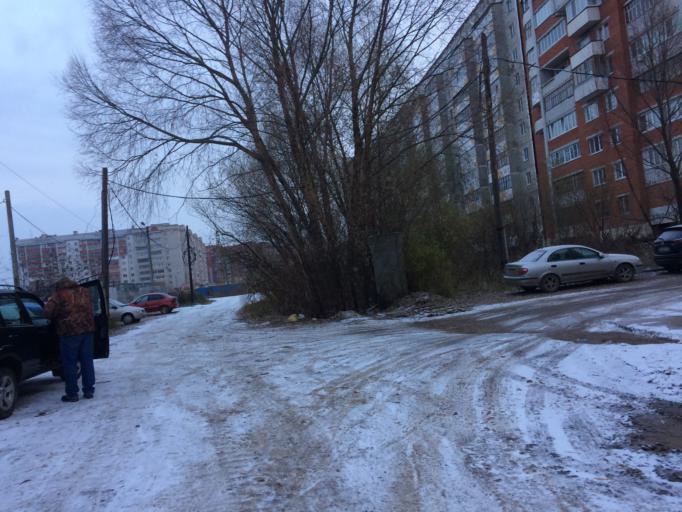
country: RU
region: Mariy-El
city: Yoshkar-Ola
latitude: 56.6384
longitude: 47.9301
